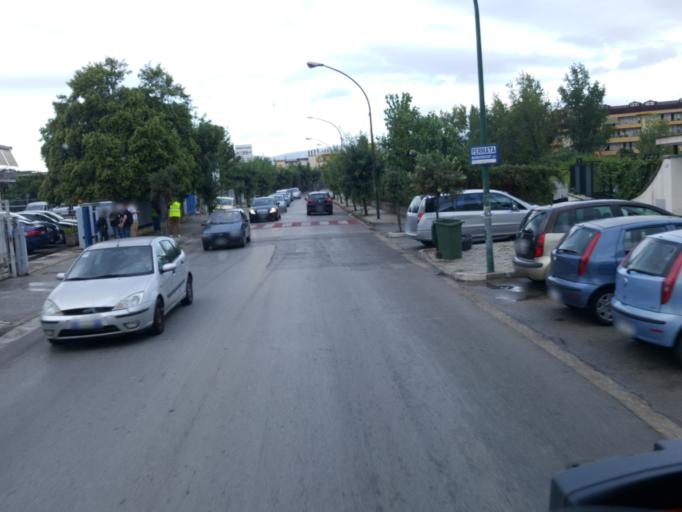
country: IT
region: Campania
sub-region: Provincia di Napoli
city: Palma Campania
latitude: 40.8690
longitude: 14.5475
